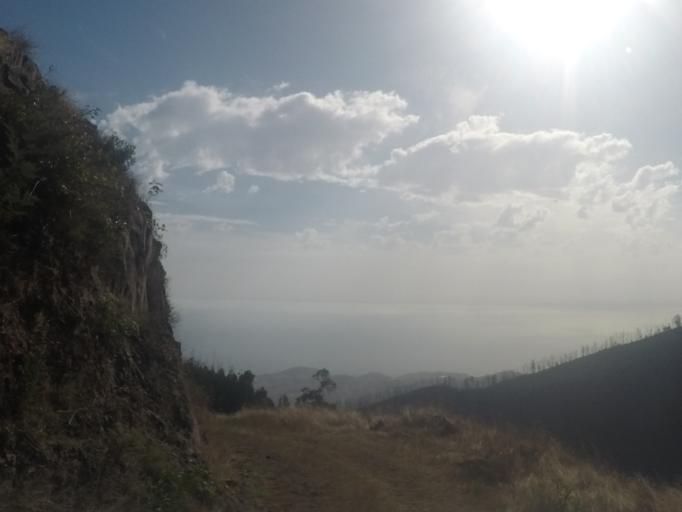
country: PT
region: Madeira
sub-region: Funchal
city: Nossa Senhora do Monte
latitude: 32.6955
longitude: -16.9120
